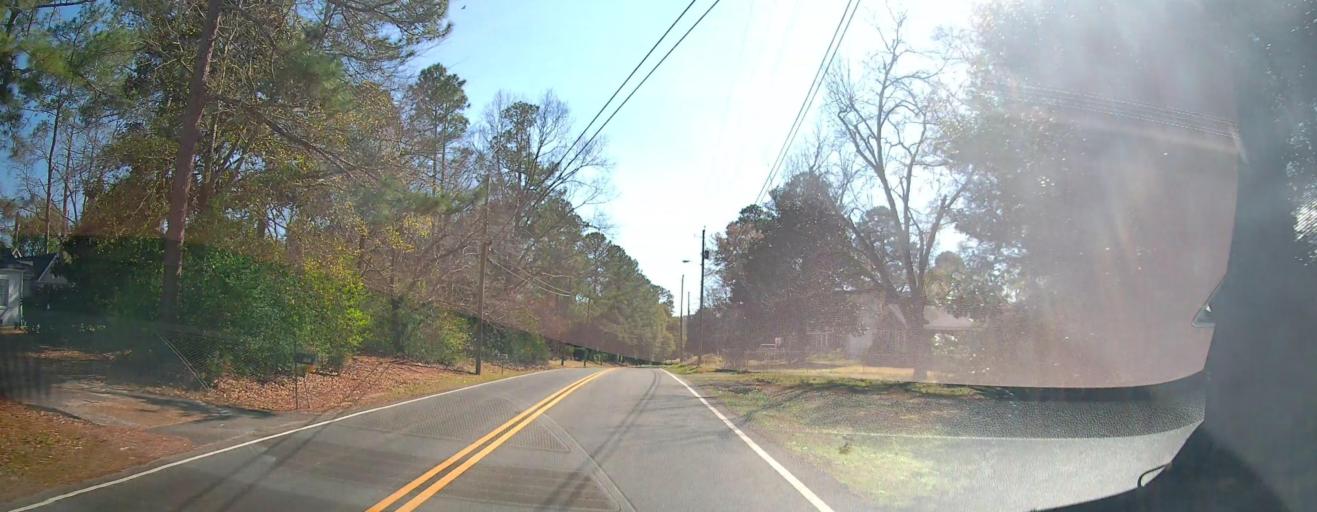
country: US
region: Georgia
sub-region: Macon County
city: Montezuma
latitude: 32.3155
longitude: -84.0239
